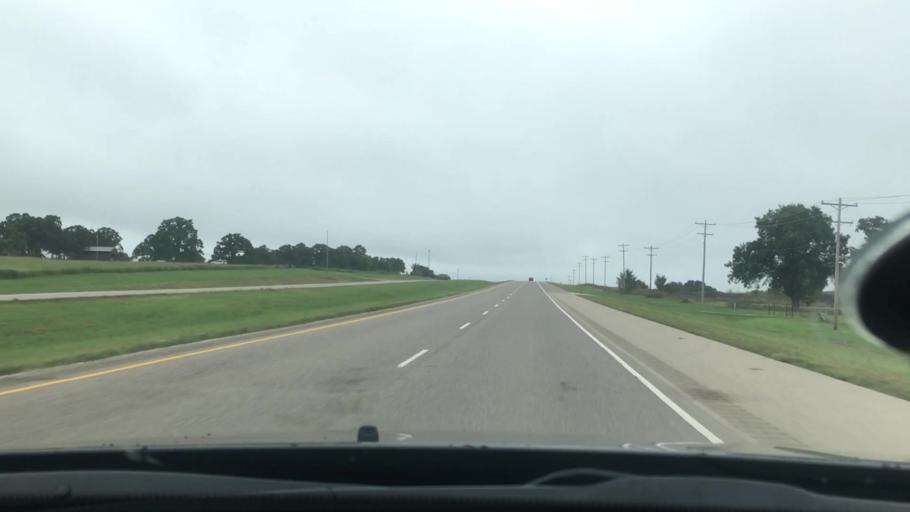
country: US
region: Oklahoma
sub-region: Lincoln County
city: Prague
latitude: 35.3654
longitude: -96.6714
